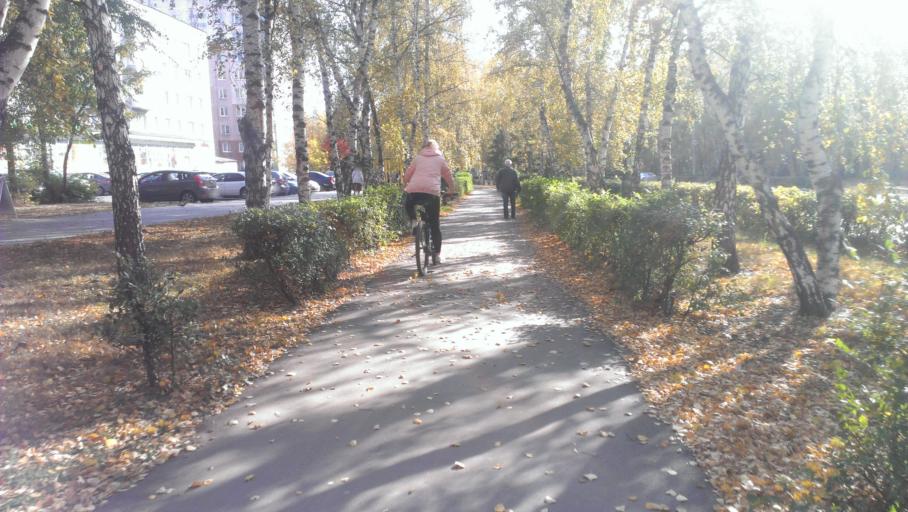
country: RU
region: Altai Krai
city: Novosilikatnyy
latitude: 53.3497
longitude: 83.6834
